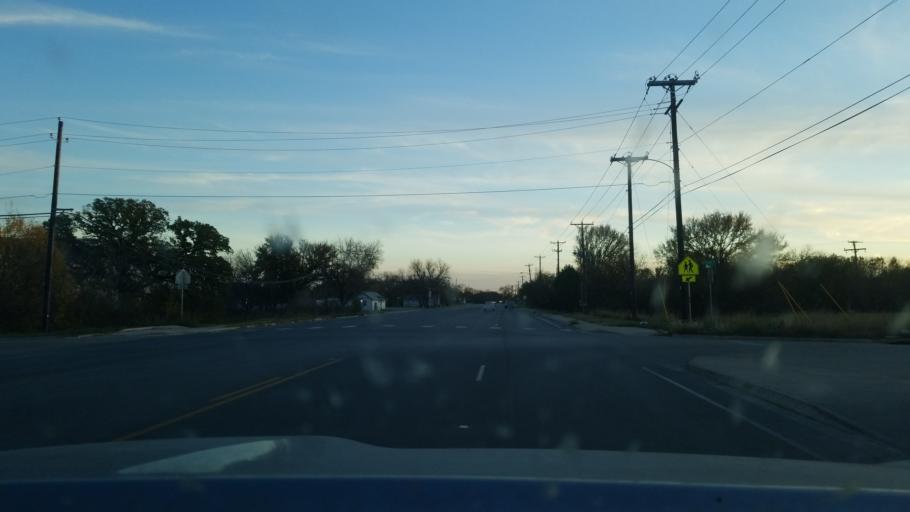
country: US
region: Texas
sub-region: Stephens County
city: Breckenridge
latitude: 32.7521
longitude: -98.9027
